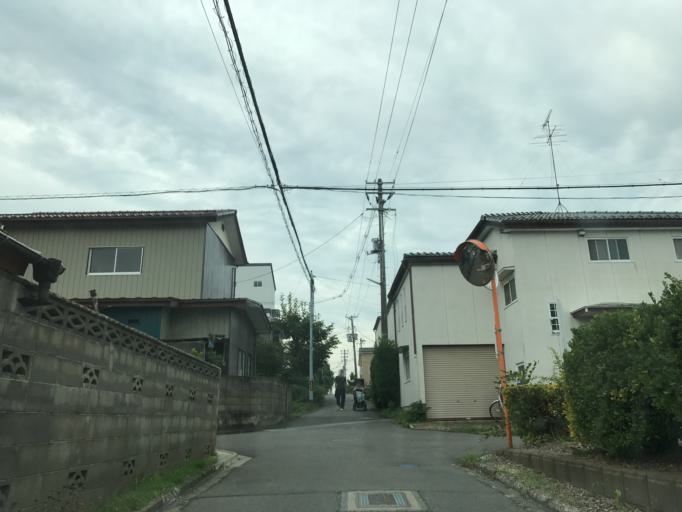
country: JP
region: Fukushima
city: Koriyama
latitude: 37.4116
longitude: 140.3696
